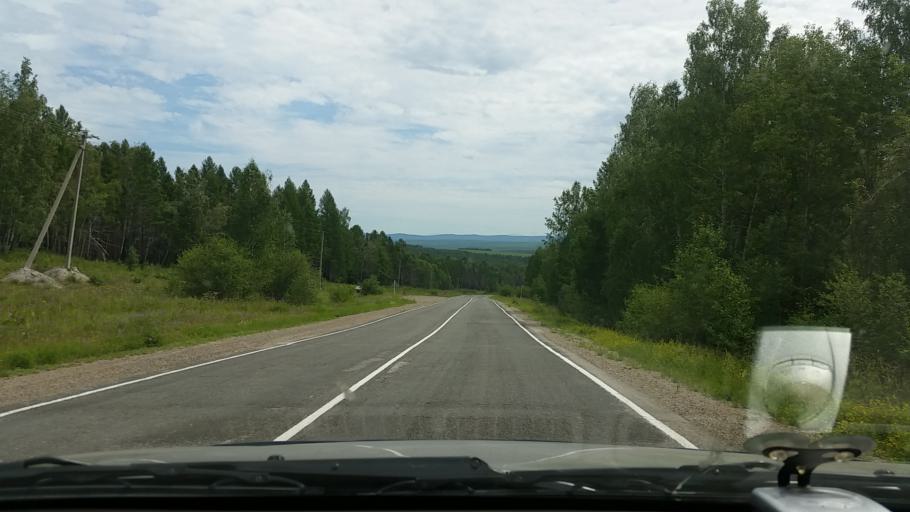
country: RU
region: Irkutsk
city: Bayanday
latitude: 53.0297
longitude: 105.6010
